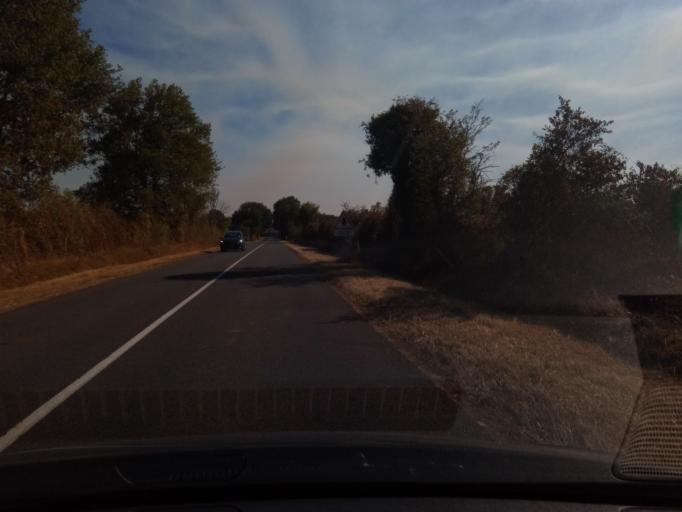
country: FR
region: Poitou-Charentes
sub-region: Departement de la Vienne
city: Montmorillon
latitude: 46.4883
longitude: 0.7863
